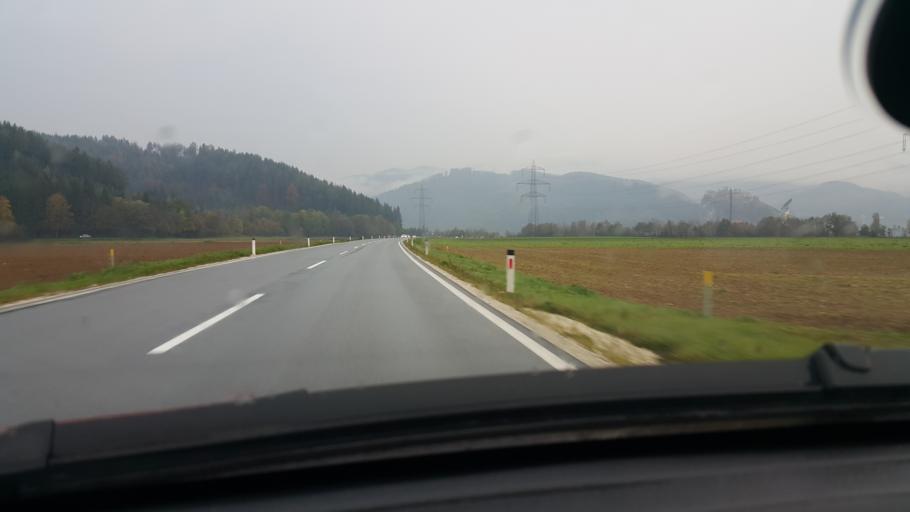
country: AT
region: Carinthia
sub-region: Politischer Bezirk Volkermarkt
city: Griffen
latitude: 46.6910
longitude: 14.7422
